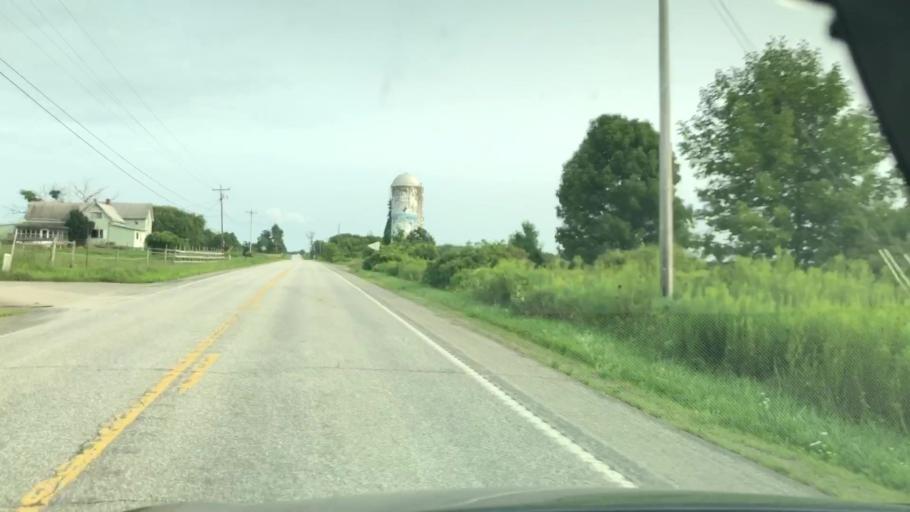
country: US
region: Pennsylvania
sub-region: Erie County
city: Union City
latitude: 41.8666
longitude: -79.8352
